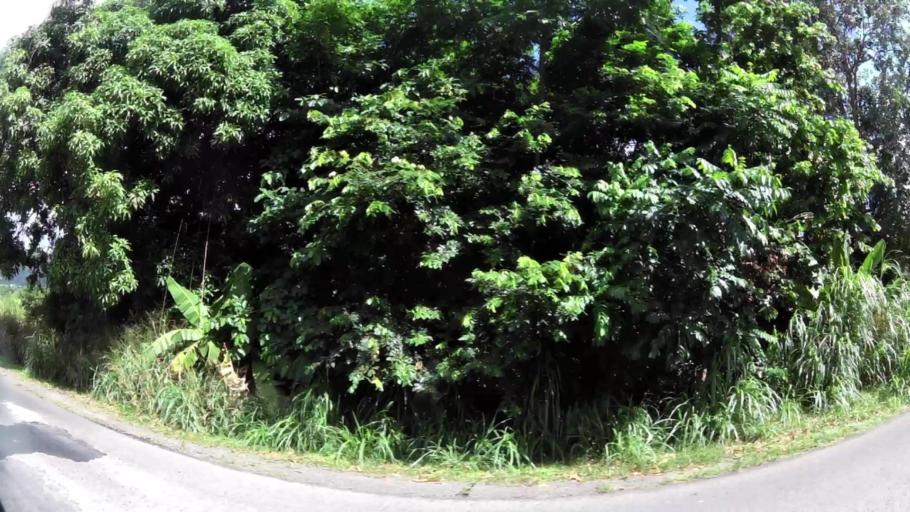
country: LC
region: Dennery Quarter
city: Dennery
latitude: 13.9349
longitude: -60.9136
